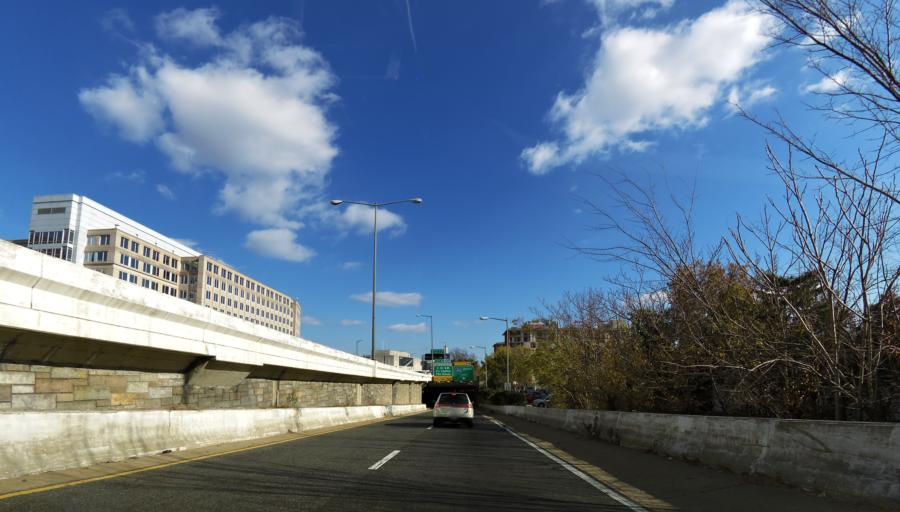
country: US
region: Washington, D.C.
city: Washington, D.C.
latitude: 38.8825
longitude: -77.0152
